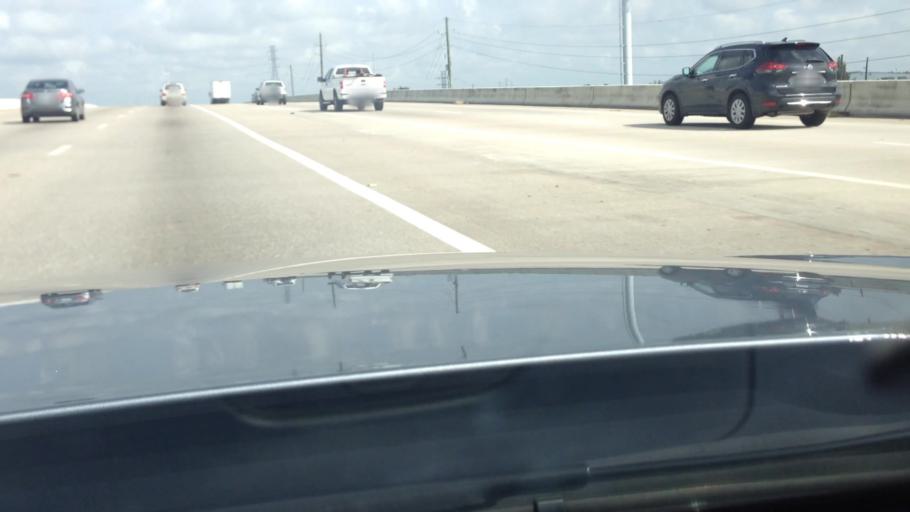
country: US
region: Texas
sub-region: Harris County
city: Hudson
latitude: 29.9436
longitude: -95.5248
